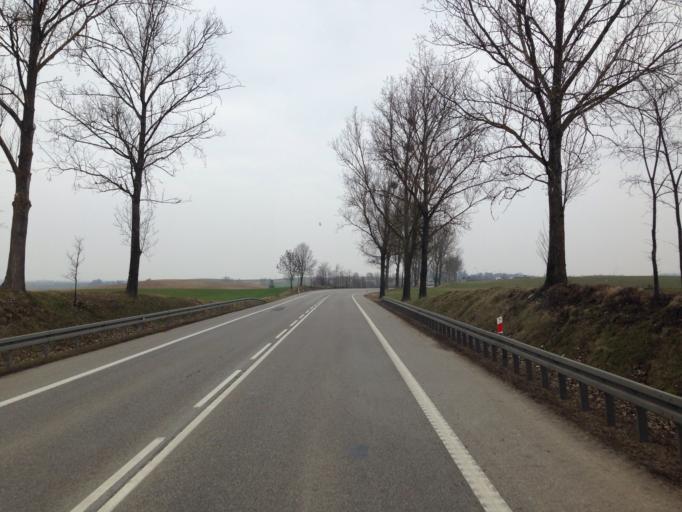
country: PL
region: Pomeranian Voivodeship
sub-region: Powiat starogardzki
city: Smetowo Graniczne
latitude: 53.7692
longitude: 18.7687
